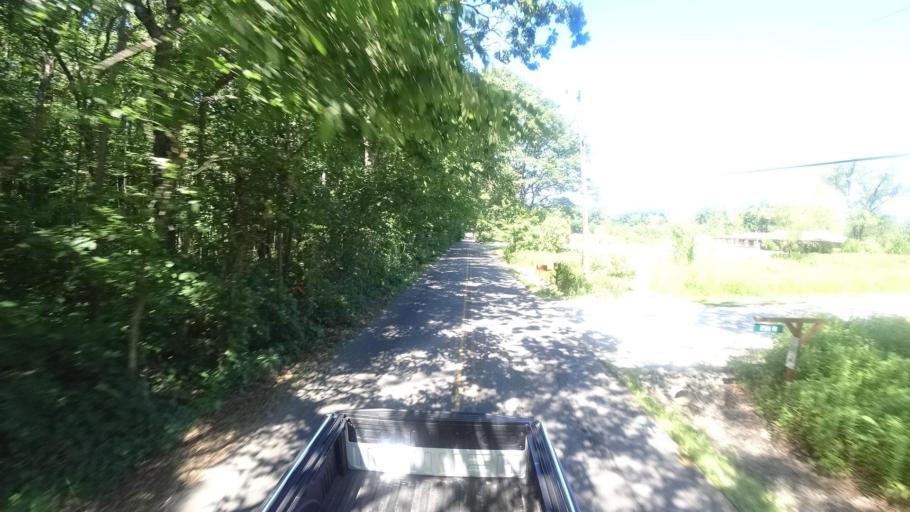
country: US
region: Indiana
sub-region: Porter County
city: Porter
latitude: 41.6297
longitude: -87.0823
